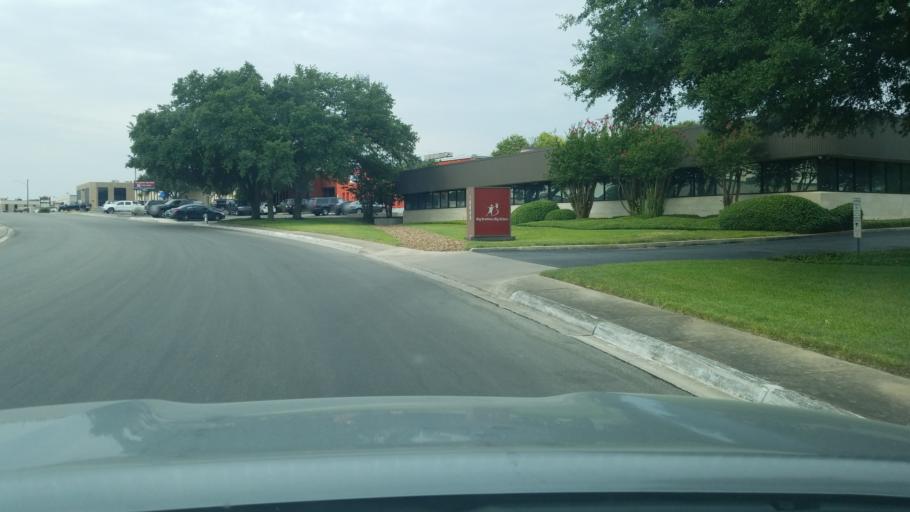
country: US
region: Texas
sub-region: Bexar County
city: Castle Hills
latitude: 29.5408
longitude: -98.4905
